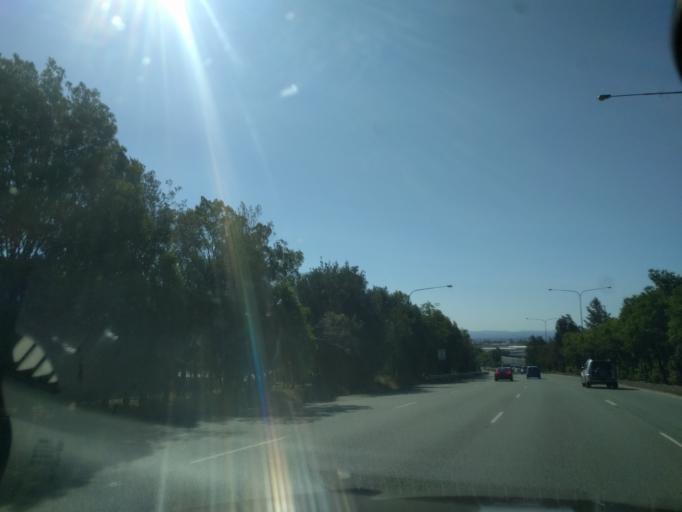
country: AU
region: Queensland
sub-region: Brisbane
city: Sunnybank
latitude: -27.5985
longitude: 153.0393
